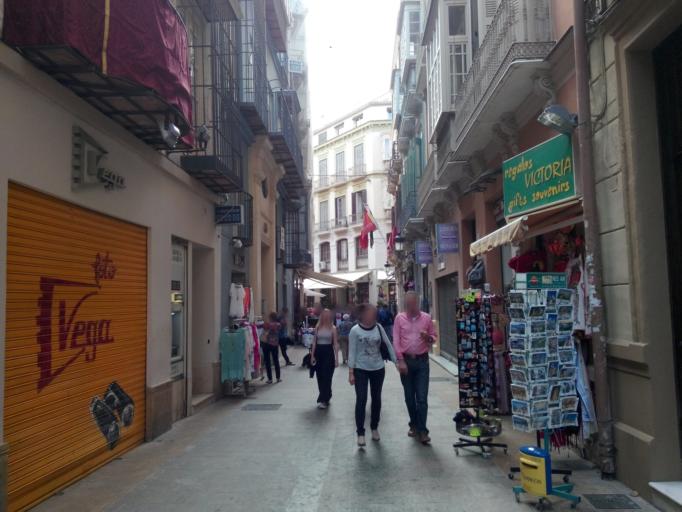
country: ES
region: Andalusia
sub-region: Provincia de Malaga
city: Malaga
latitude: 36.7220
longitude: -4.4186
